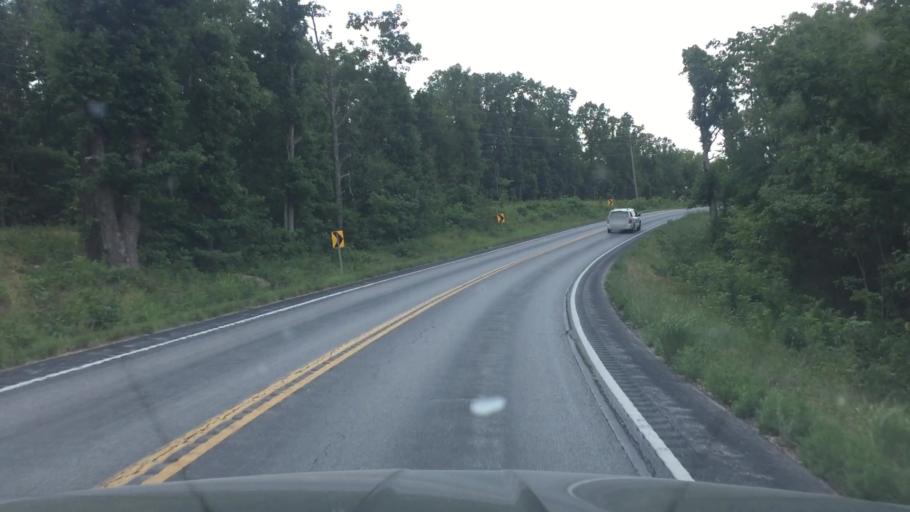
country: US
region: Missouri
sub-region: Miller County
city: Tuscumbia
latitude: 38.0967
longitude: -92.4961
